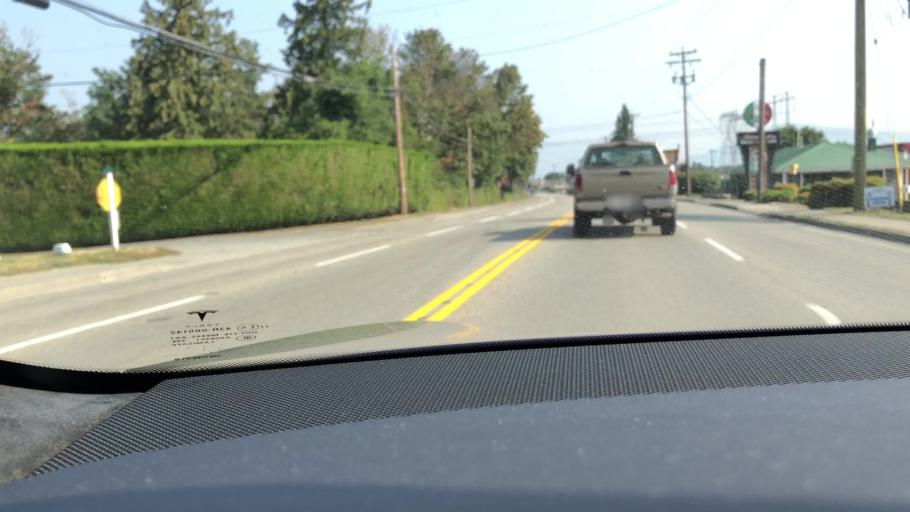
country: CA
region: British Columbia
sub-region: Fraser Valley Regional District
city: Chilliwack
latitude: 49.1124
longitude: -121.9577
